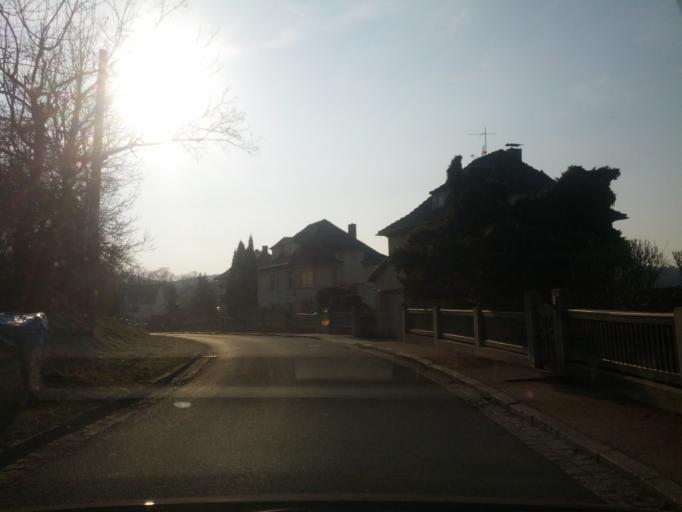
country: DE
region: Thuringia
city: Eisenach
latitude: 50.9663
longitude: 10.3300
